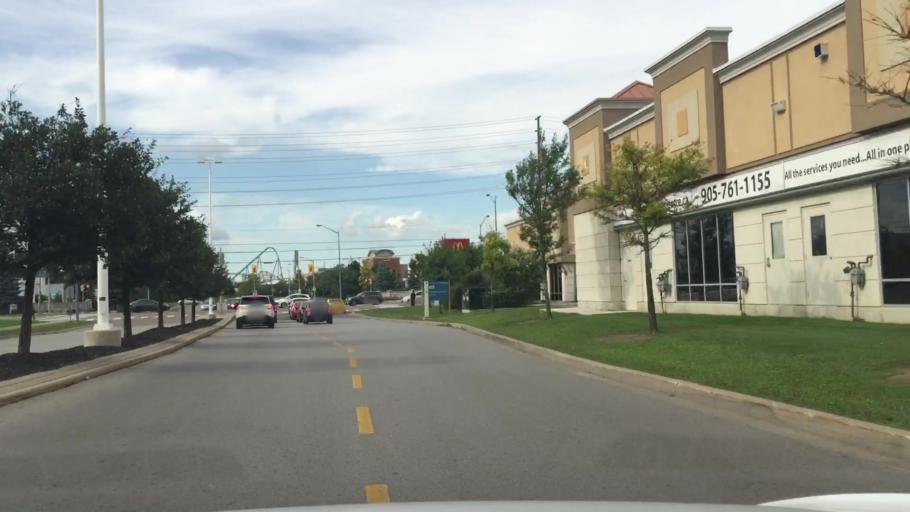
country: CA
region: Ontario
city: Vaughan
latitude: 43.8291
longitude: -79.5354
